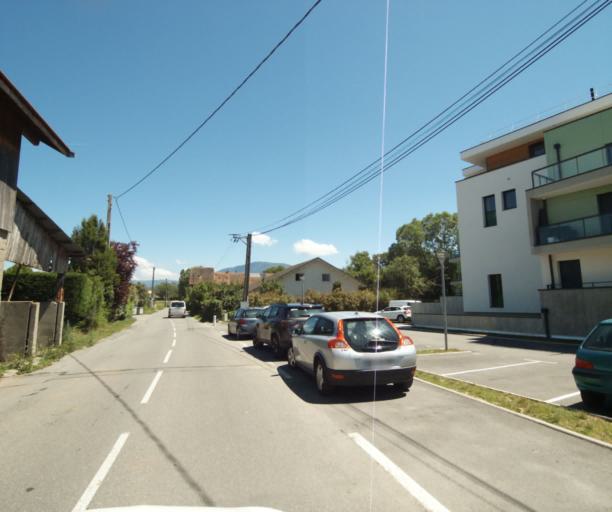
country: FR
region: Rhone-Alpes
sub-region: Departement de la Haute-Savoie
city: Veigy-Foncenex
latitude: 46.2641
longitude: 6.2531
